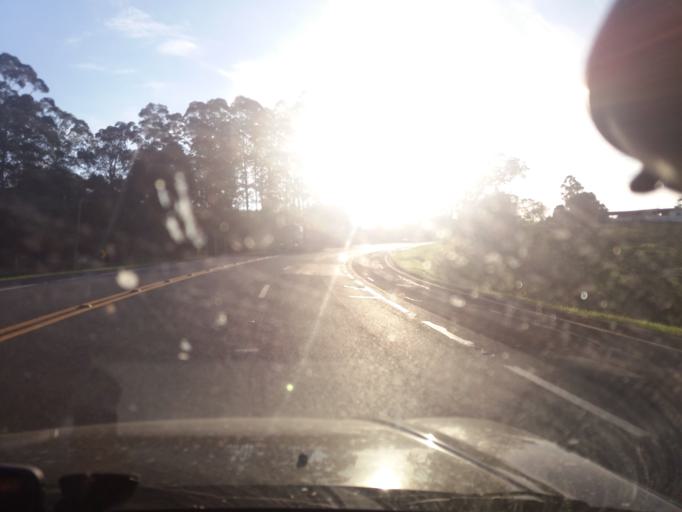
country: BR
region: Sao Paulo
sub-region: Buri
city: Buri
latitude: -23.9291
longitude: -48.6678
